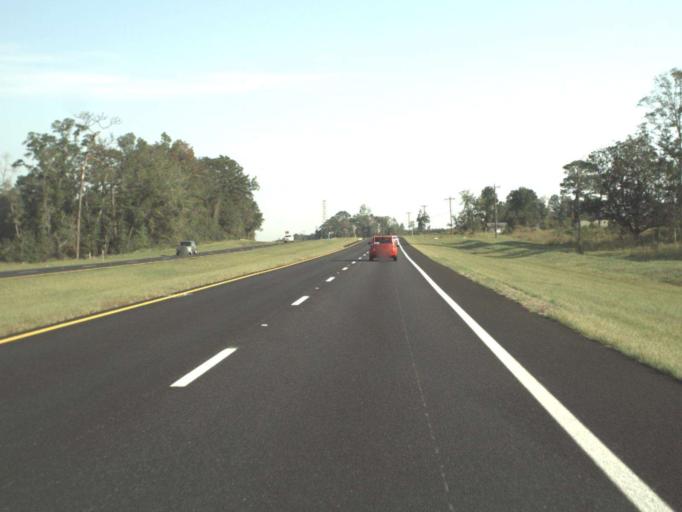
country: US
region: Florida
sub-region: Bay County
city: Laguna Beach
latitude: 30.4839
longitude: -85.8430
